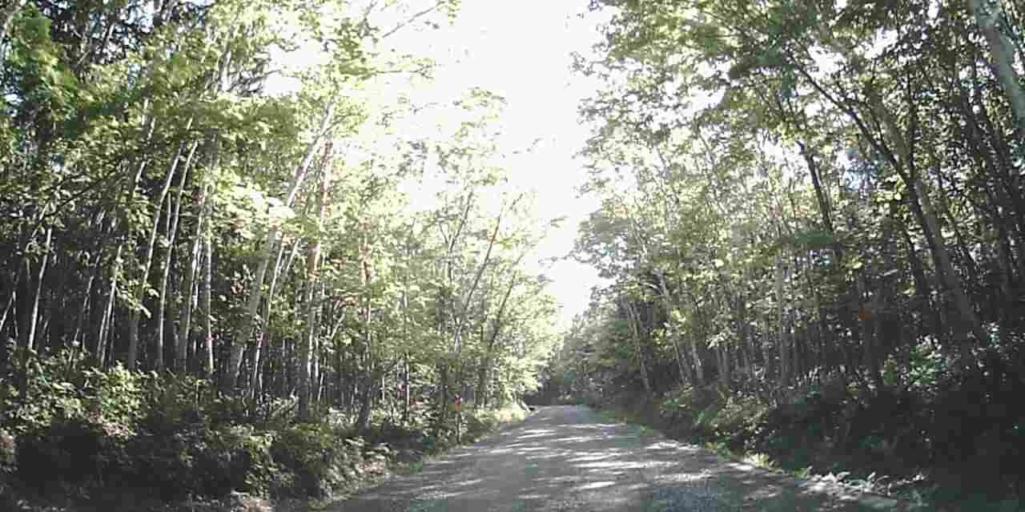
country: JP
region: Hokkaido
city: Shiraoi
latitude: 42.7131
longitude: 141.4007
